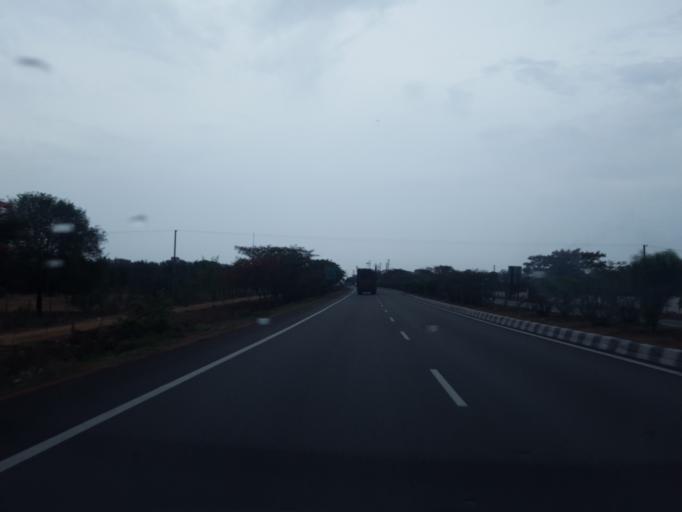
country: IN
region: Telangana
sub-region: Mahbubnagar
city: Farrukhnagar
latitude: 17.1400
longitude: 78.2885
